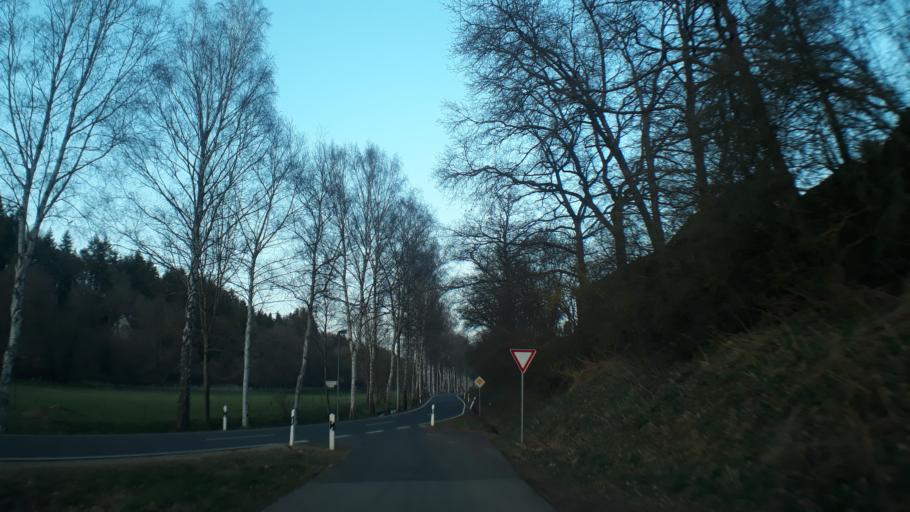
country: DE
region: Rheinland-Pfalz
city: Hummel
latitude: 50.5087
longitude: 6.7681
